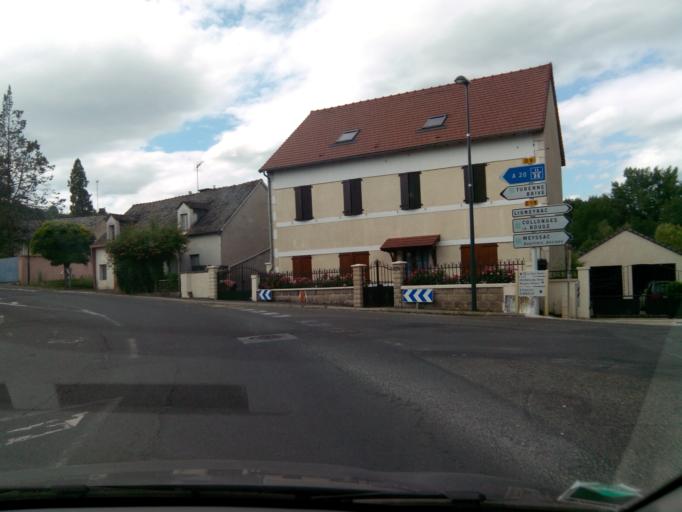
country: FR
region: Limousin
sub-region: Departement de la Correze
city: Meyssac
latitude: 45.0364
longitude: 1.6027
